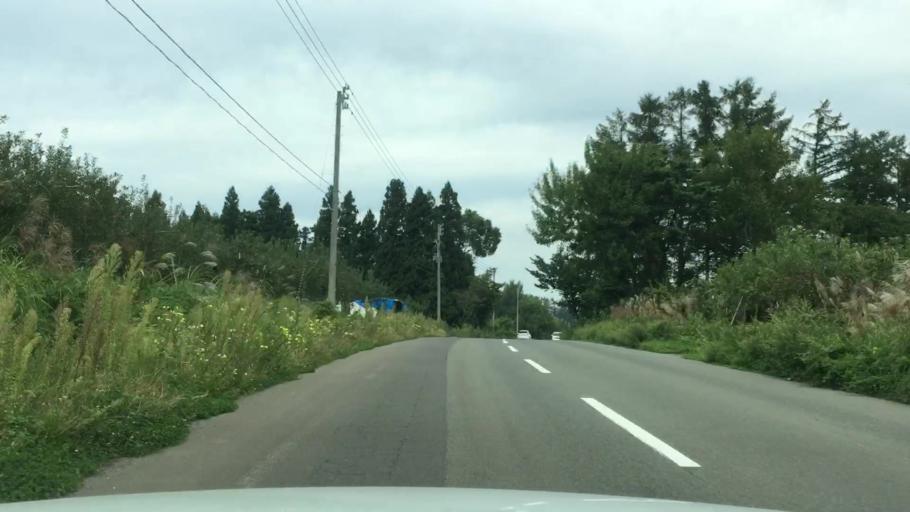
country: JP
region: Aomori
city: Hirosaki
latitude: 40.6806
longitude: 140.3715
